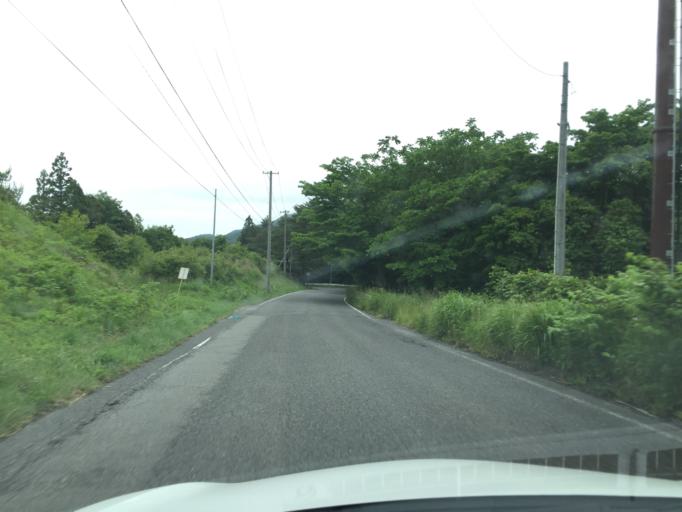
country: JP
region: Fukushima
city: Funehikimachi-funehiki
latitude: 37.3231
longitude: 140.7027
